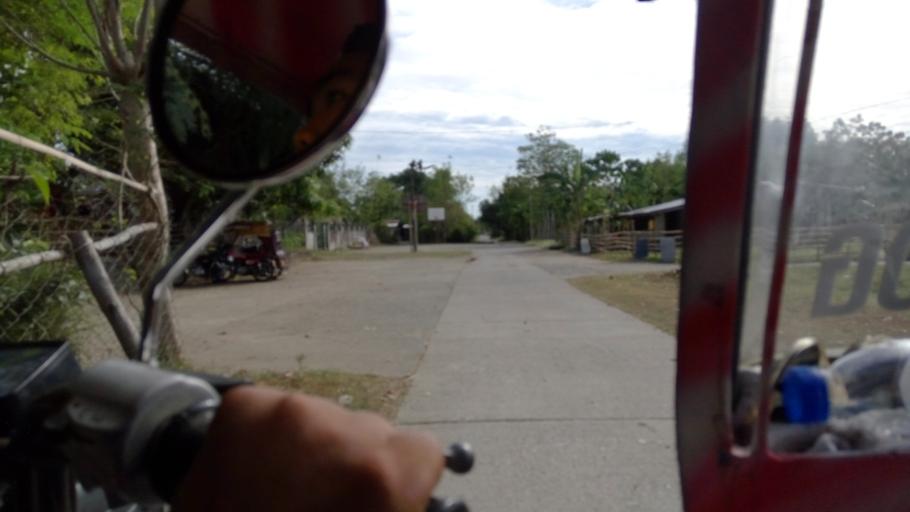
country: PH
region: Ilocos
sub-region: Province of La Union
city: San Eugenio
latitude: 16.3749
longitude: 120.3523
